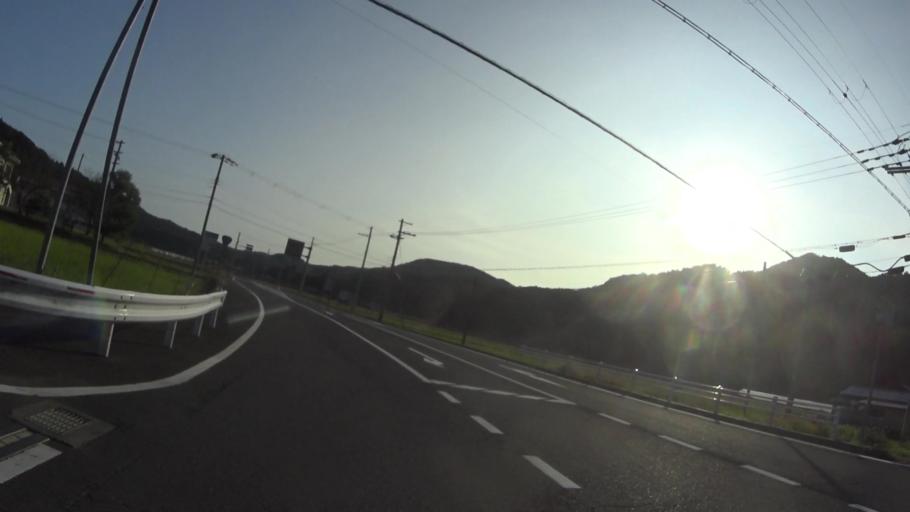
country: JP
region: Kyoto
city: Miyazu
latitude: 35.7300
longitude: 135.2559
